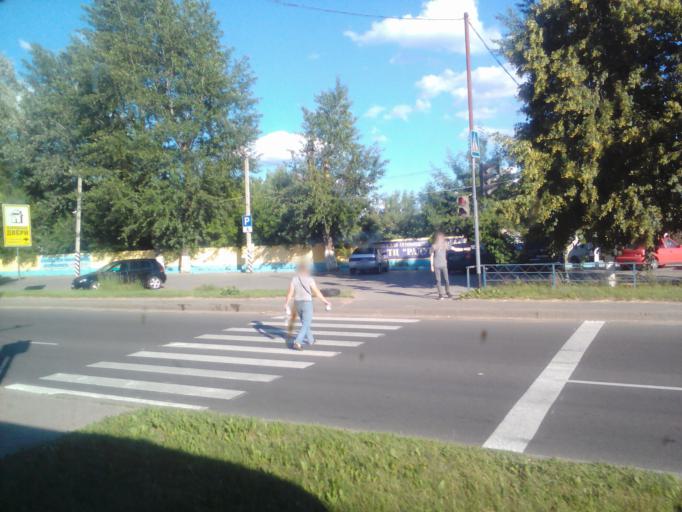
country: RU
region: Kursk
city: Kursk
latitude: 51.7050
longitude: 36.1712
